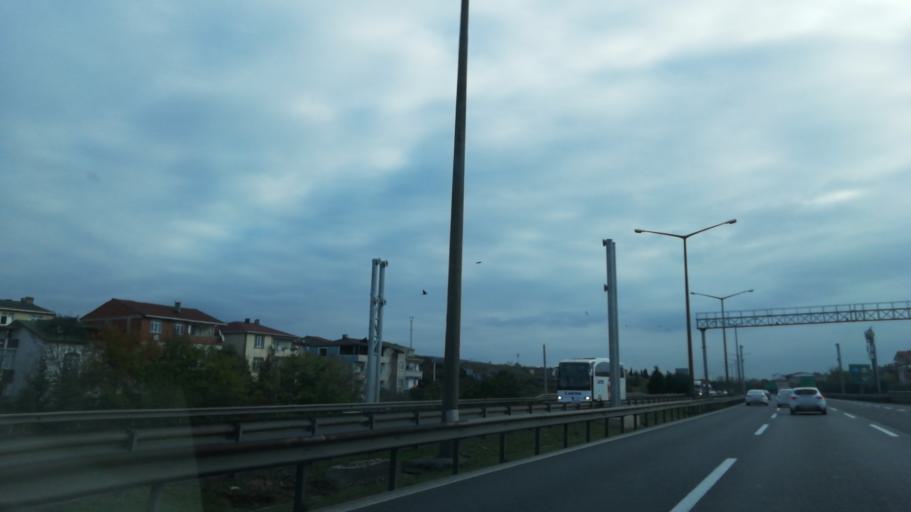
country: TR
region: Kocaeli
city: Korfez
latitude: 40.7711
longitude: 29.7760
